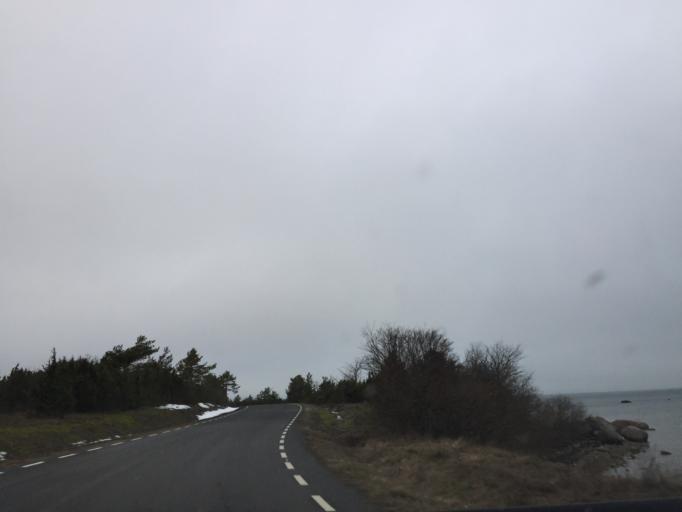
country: EE
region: Saare
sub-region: Kuressaare linn
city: Kuressaare
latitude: 58.5649
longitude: 22.3108
